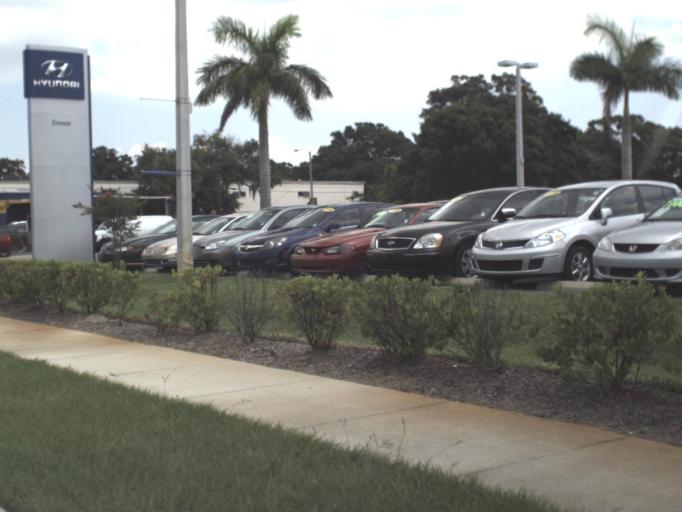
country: US
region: Florida
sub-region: Pinellas County
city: Lealman
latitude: 27.8206
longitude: -82.6794
